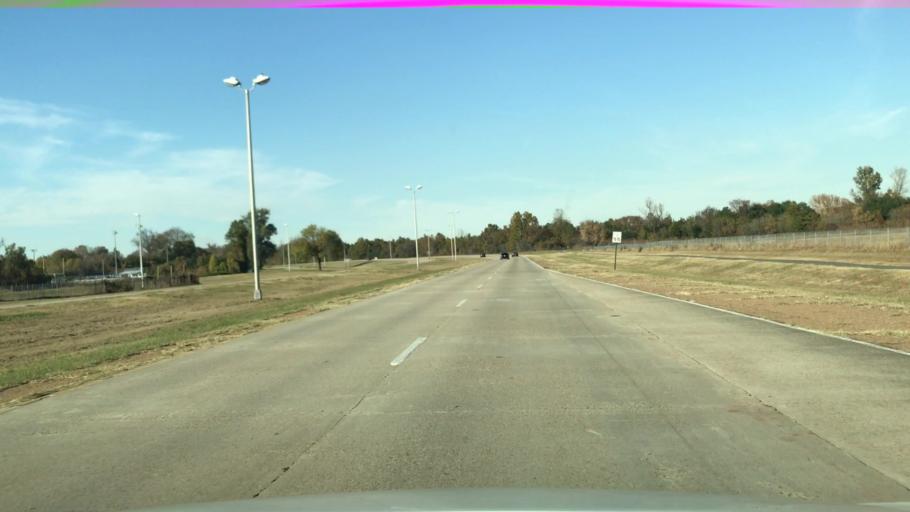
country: US
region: Louisiana
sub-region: Bossier Parish
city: Bossier City
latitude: 32.4807
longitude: -93.6930
